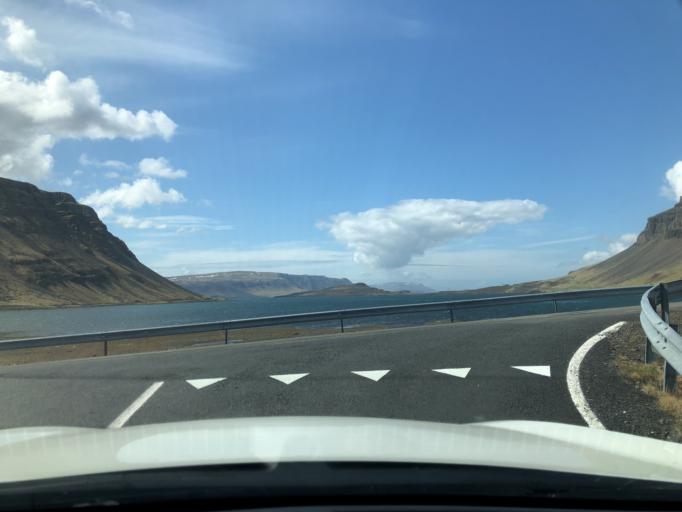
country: IS
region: Capital Region
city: Mosfellsbaer
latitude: 64.3858
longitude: -21.3549
